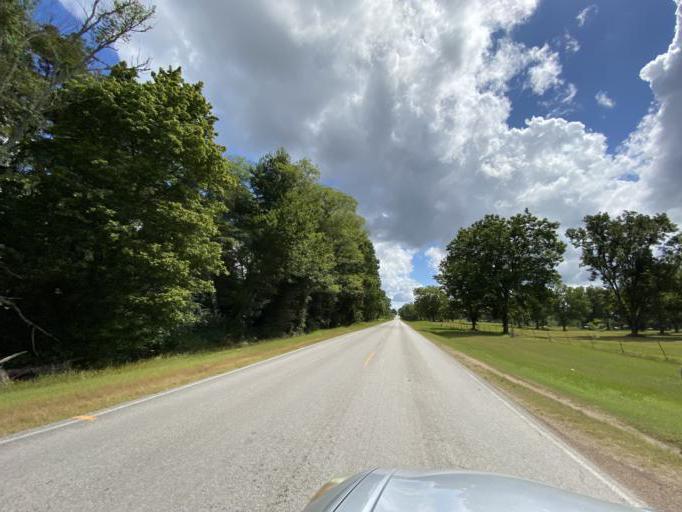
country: US
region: Mississippi
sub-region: Panola County
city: Como
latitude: 34.5104
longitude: -90.0004
